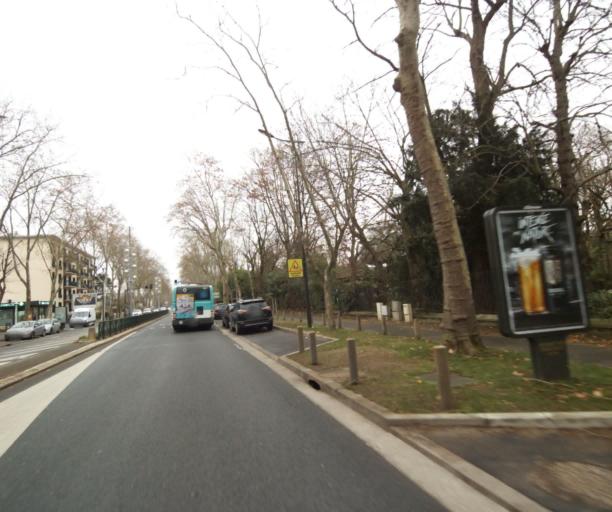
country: FR
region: Ile-de-France
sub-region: Departement des Yvelines
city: Chatou
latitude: 48.8727
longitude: 2.1635
